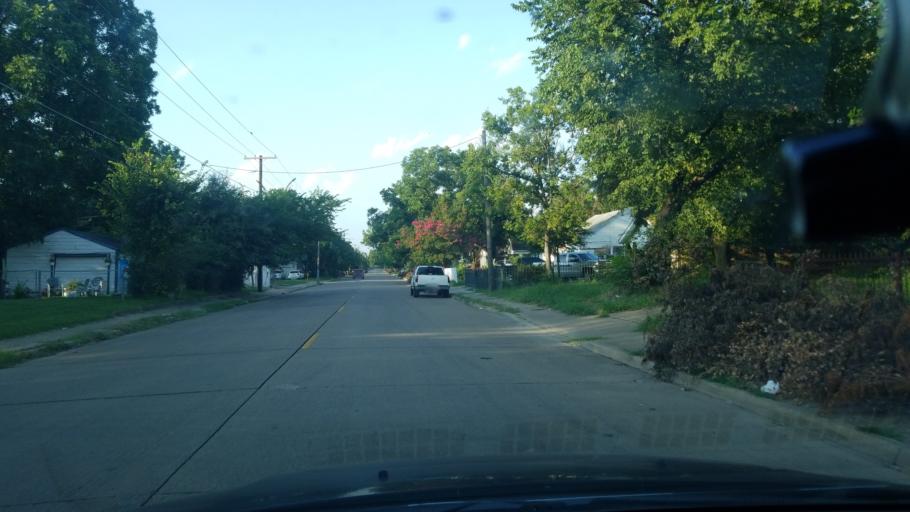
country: US
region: Texas
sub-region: Dallas County
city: Balch Springs
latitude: 32.7324
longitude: -96.6786
